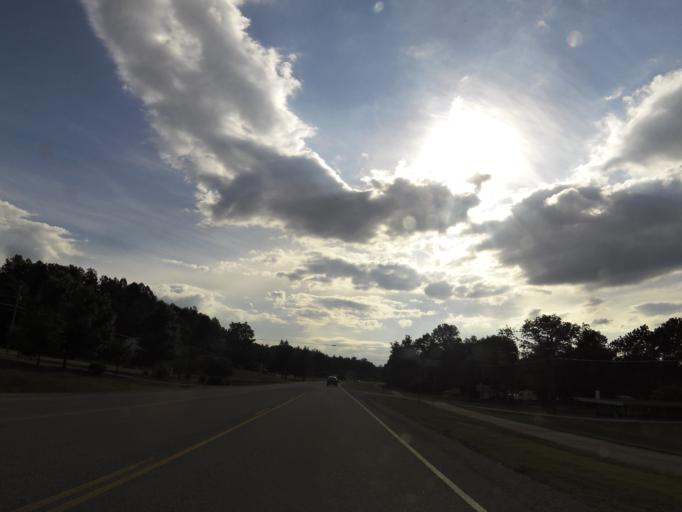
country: US
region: Tennessee
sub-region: Blount County
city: Wildwood
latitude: 35.6787
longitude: -83.7258
